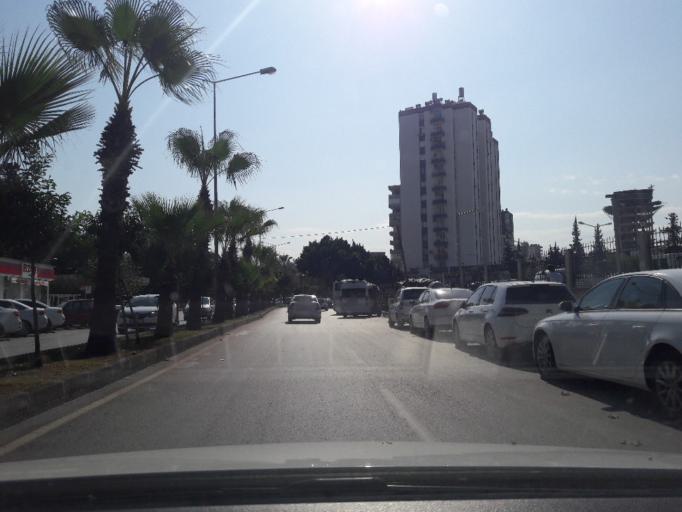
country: TR
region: Adana
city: Adana
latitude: 37.0197
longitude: 35.3201
